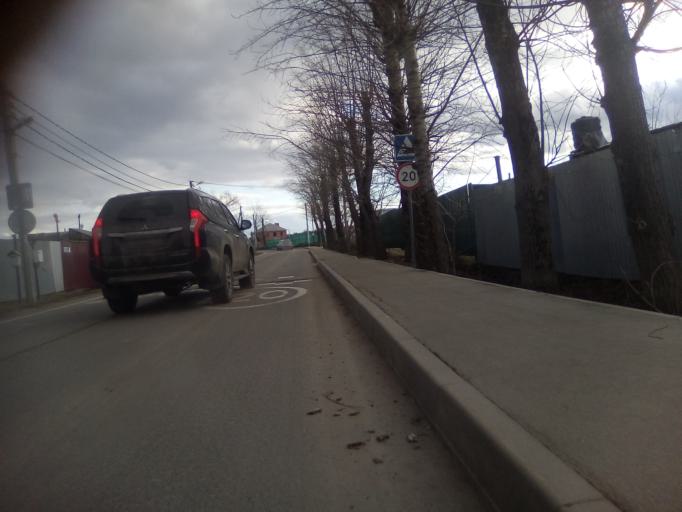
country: RU
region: Moskovskaya
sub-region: Leninskiy Rayon
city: Vnukovo
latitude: 55.5957
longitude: 37.3191
